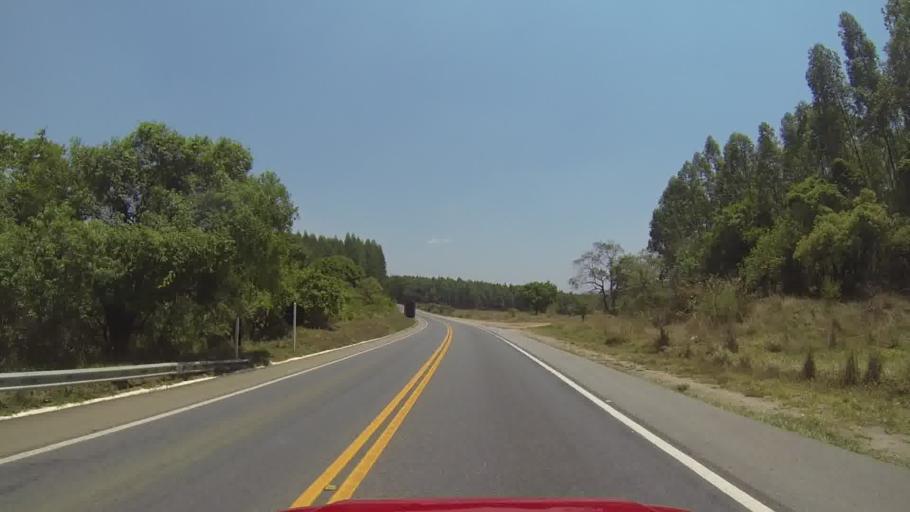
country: BR
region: Minas Gerais
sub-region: Itapecerica
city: Itapecerica
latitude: -20.3074
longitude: -45.2109
